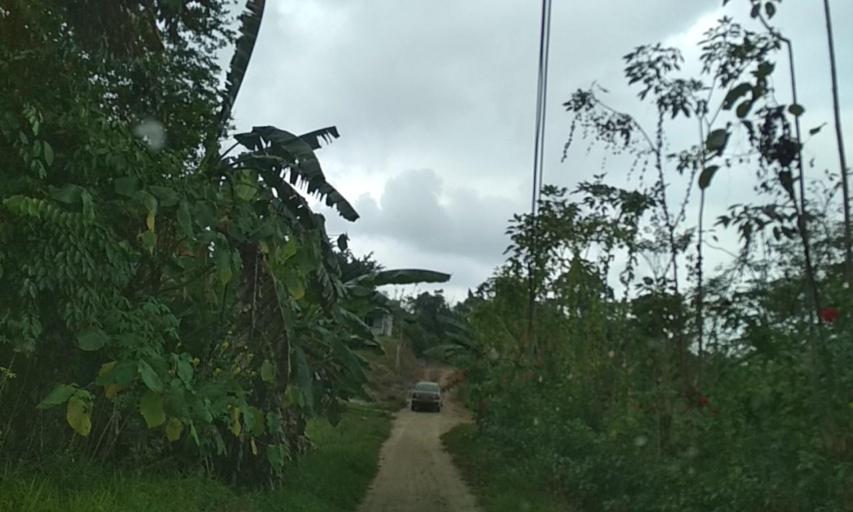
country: MX
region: Veracruz
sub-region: Uxpanapa
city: Poblado 10
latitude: 17.4579
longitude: -94.1028
